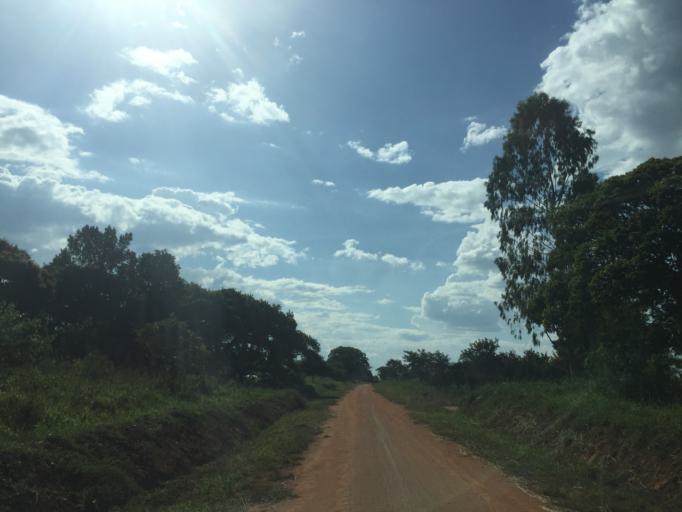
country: UG
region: Western Region
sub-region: Kiryandongo District
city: Masindi Port
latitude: 1.5282
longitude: 32.0947
